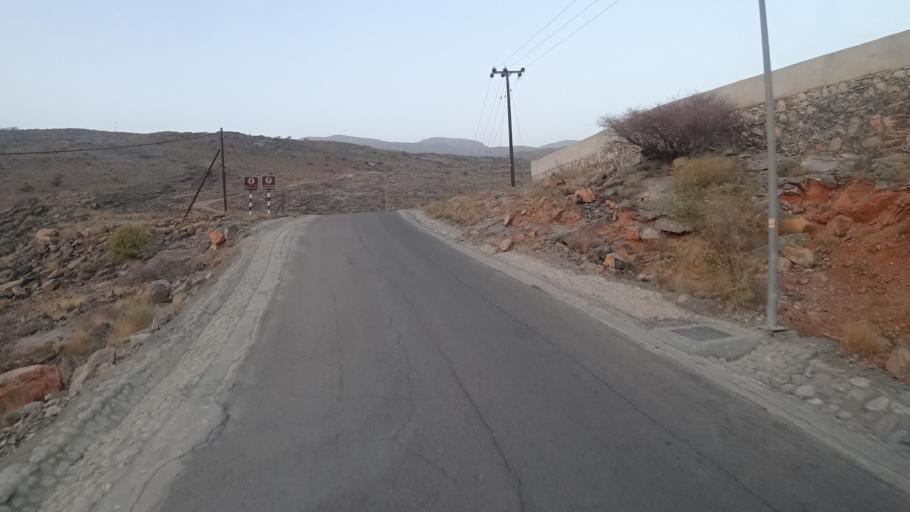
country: OM
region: Muhafazat ad Dakhiliyah
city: Bahla'
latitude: 23.1394
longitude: 57.3069
